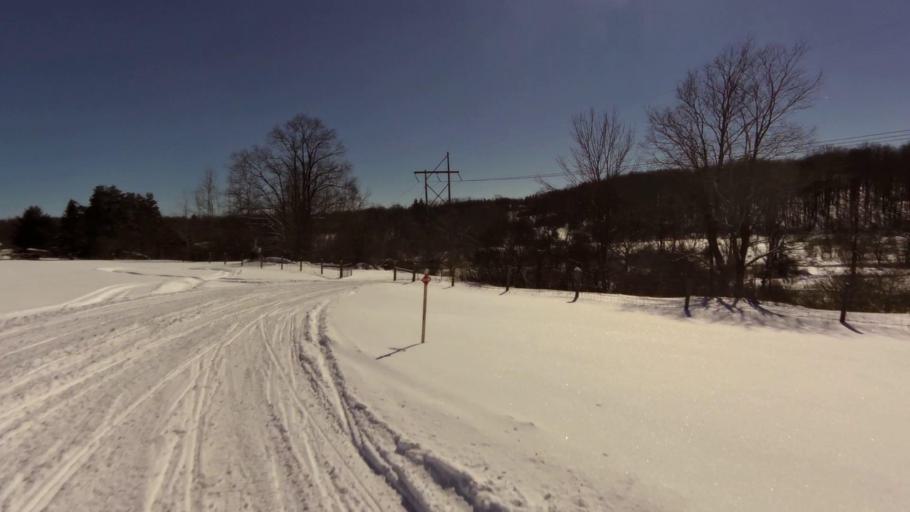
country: US
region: New York
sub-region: Chautauqua County
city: Mayville
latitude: 42.2266
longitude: -79.5181
